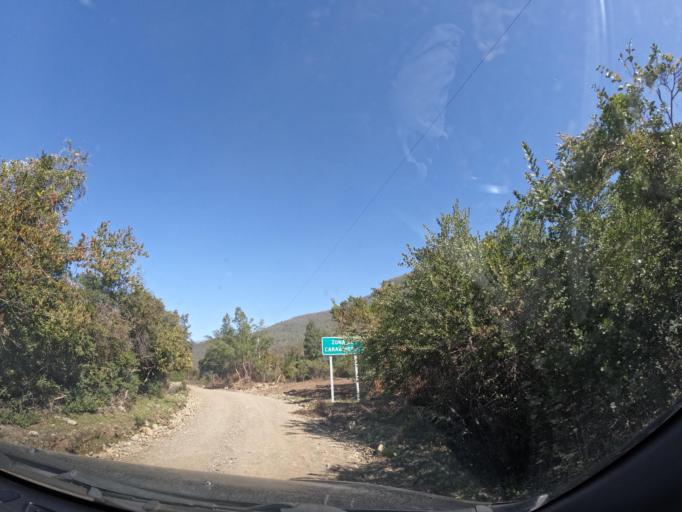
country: CL
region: Maule
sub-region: Provincia de Linares
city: Longavi
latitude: -36.2861
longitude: -71.4161
